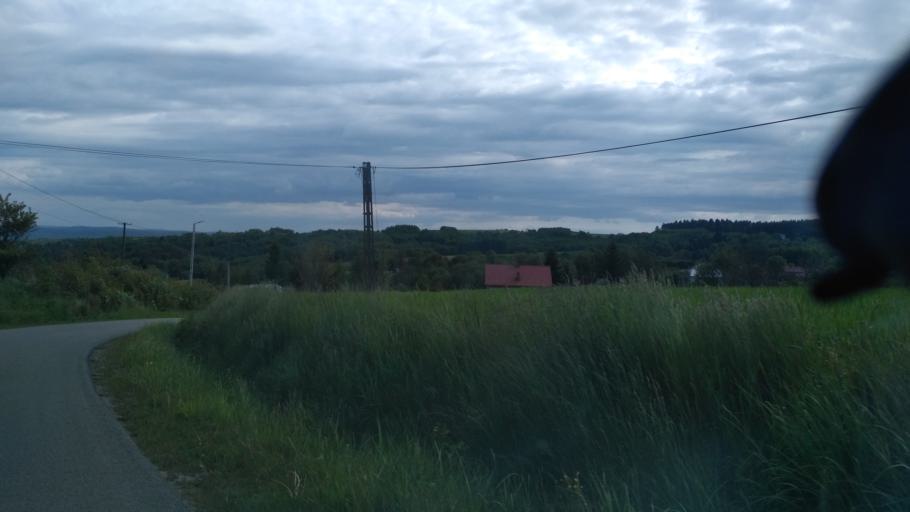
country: PL
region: Subcarpathian Voivodeship
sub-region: Powiat przemyski
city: Nienadowa
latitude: 49.8783
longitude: 22.4175
